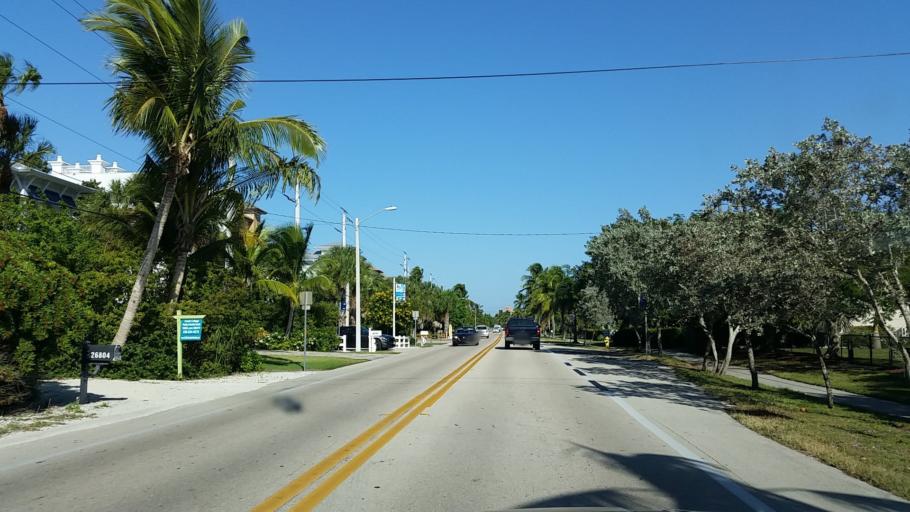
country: US
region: Florida
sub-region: Lee County
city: Bonita Springs
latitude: 26.3472
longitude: -81.8522
